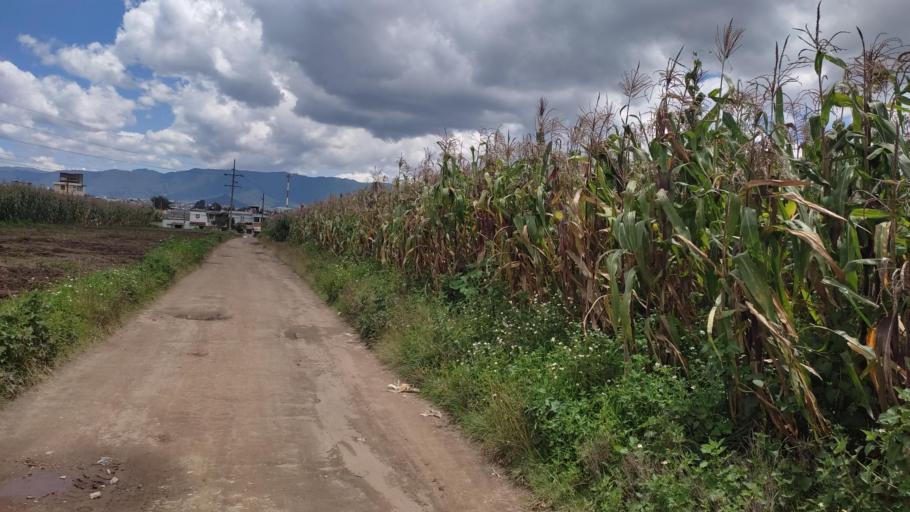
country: GT
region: Quetzaltenango
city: Quetzaltenango
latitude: 14.8585
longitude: -91.5280
